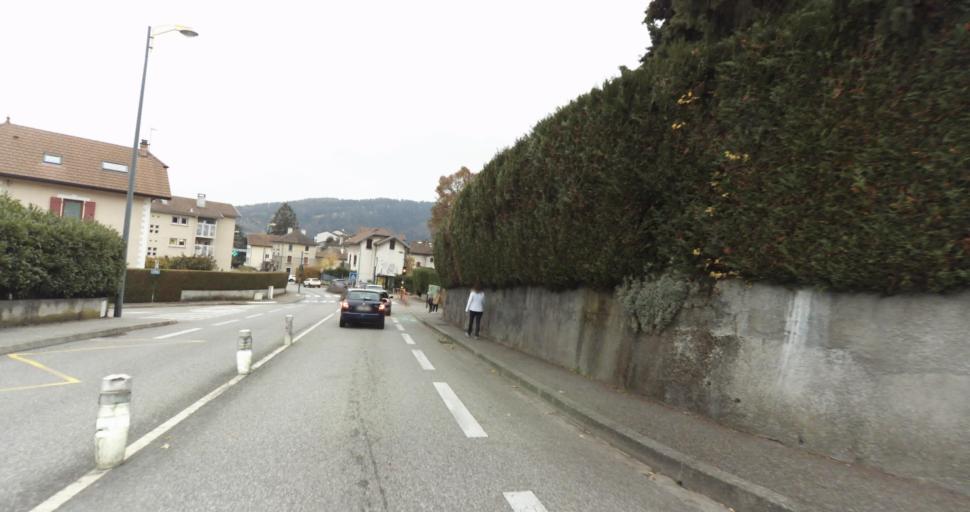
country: FR
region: Rhone-Alpes
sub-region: Departement de la Haute-Savoie
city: Annecy
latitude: 45.8993
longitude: 6.1095
